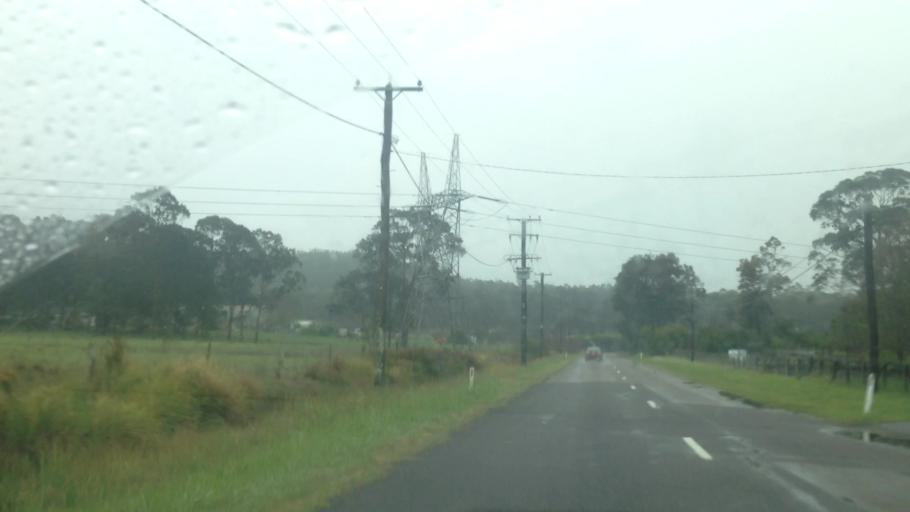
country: AU
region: New South Wales
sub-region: Wyong Shire
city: Little Jilliby
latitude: -33.2191
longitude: 151.3722
